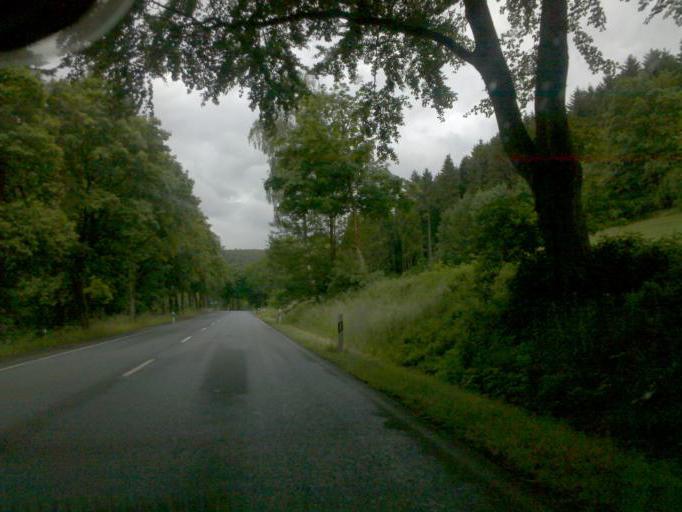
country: DE
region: North Rhine-Westphalia
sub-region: Regierungsbezirk Arnsberg
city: Meschede
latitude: 51.3360
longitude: 8.2586
